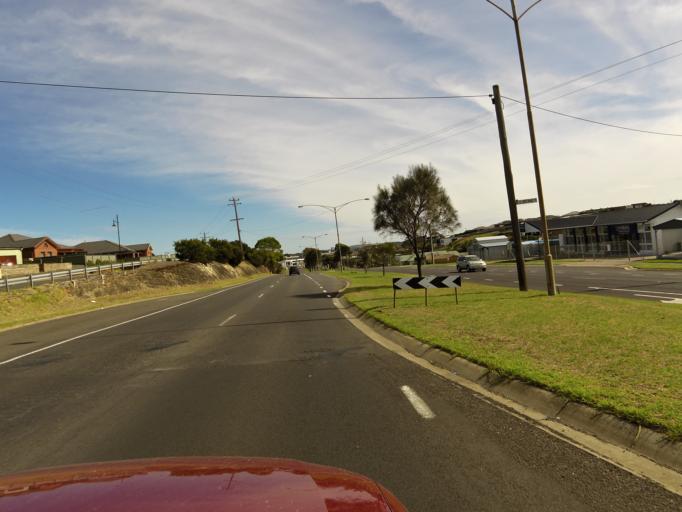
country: AU
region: Victoria
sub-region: Warrnambool
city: Warrnambool
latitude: -38.3720
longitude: 142.4741
